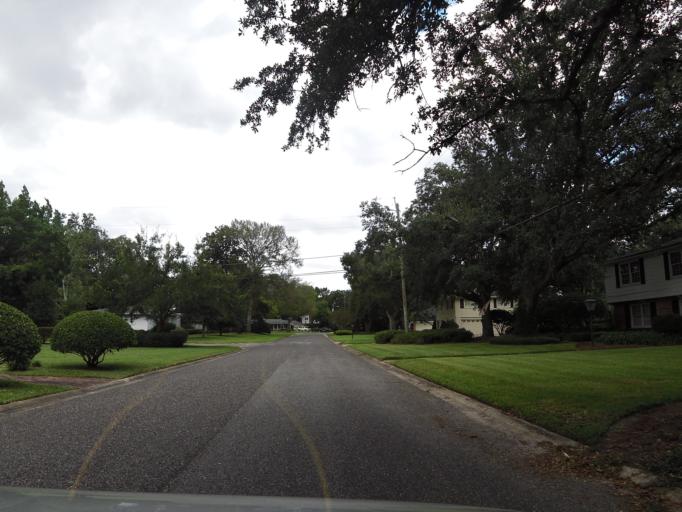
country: US
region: Florida
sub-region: Clay County
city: Bellair-Meadowbrook Terrace
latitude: 30.2561
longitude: -81.7067
